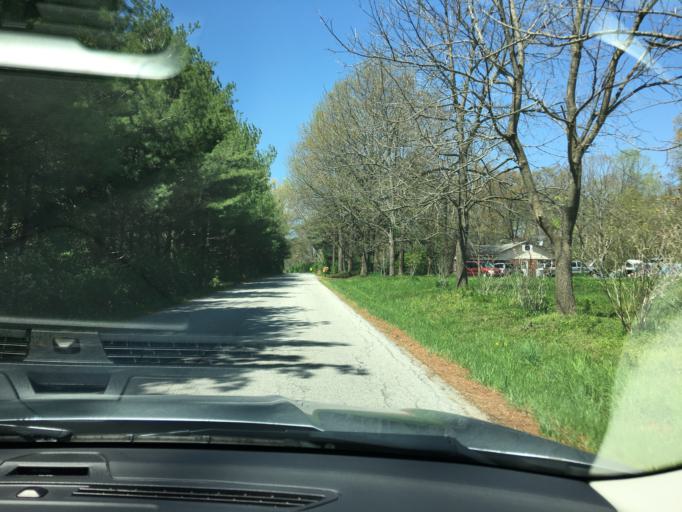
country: US
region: Indiana
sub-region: Tippecanoe County
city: Dayton
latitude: 40.3152
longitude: -86.7542
